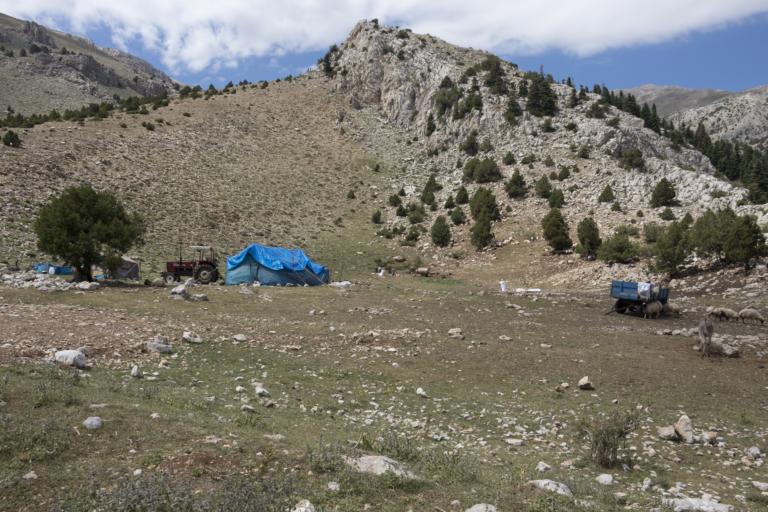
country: TR
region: Kayseri
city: Toklar
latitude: 38.3215
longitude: 36.0829
